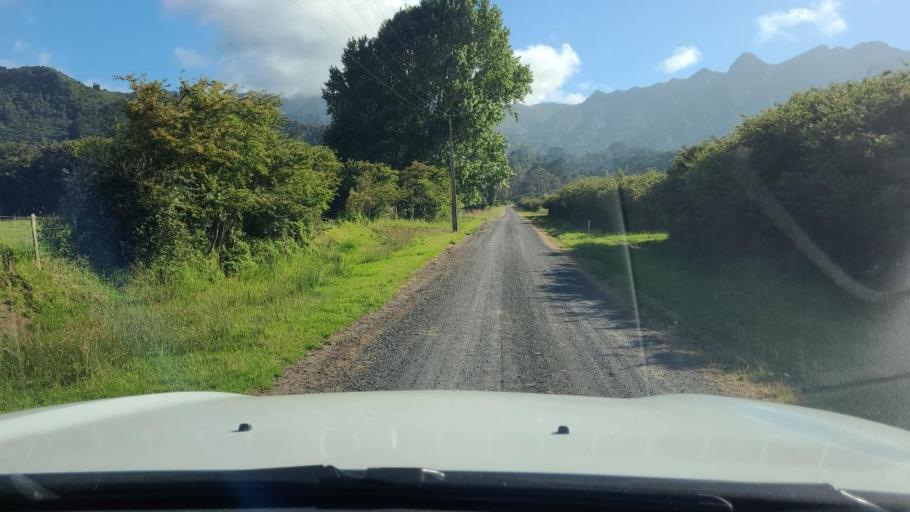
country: NZ
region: Bay of Plenty
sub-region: Western Bay of Plenty District
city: Katikati
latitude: -37.5717
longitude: 175.7637
